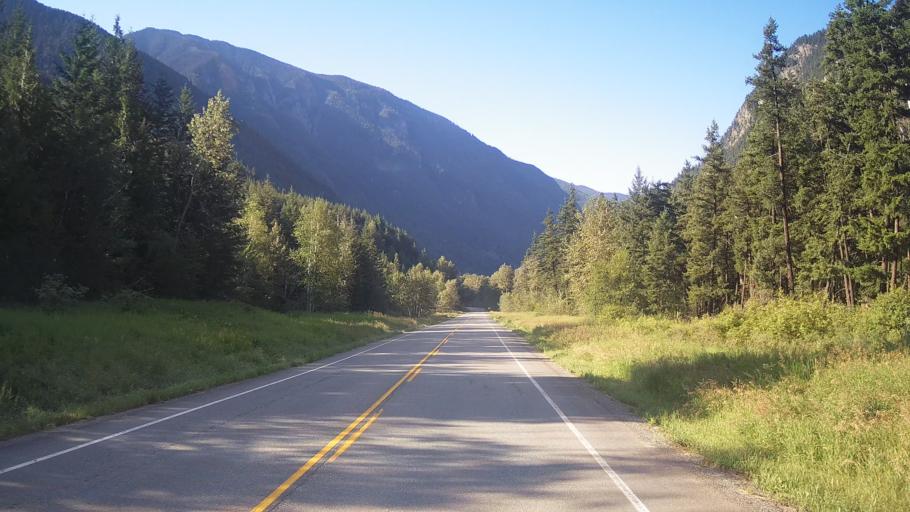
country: CA
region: British Columbia
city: Lillooet
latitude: 50.5791
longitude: -122.0878
